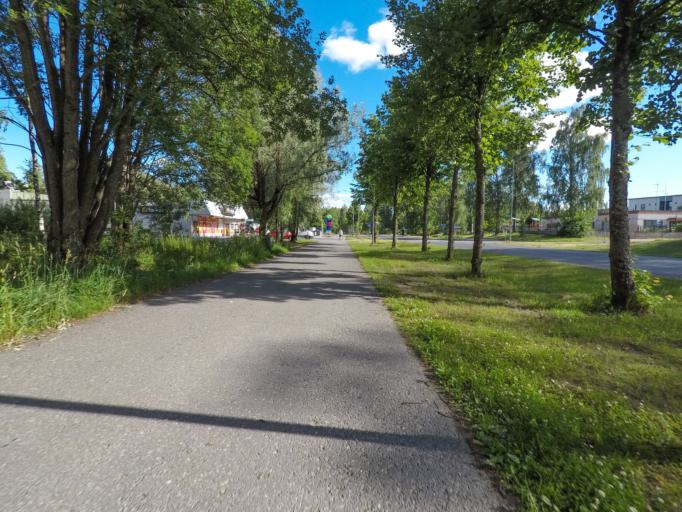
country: FI
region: South Karelia
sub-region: Lappeenranta
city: Lappeenranta
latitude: 61.0784
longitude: 28.1502
